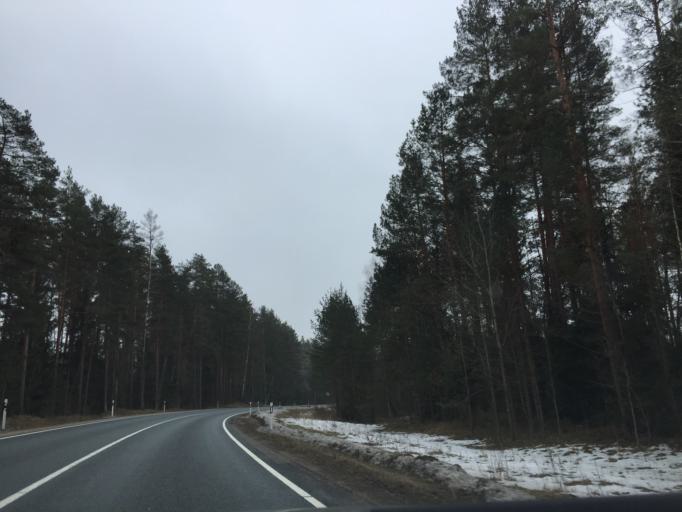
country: LV
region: Olaine
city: Olaine
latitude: 56.6221
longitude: 24.0124
